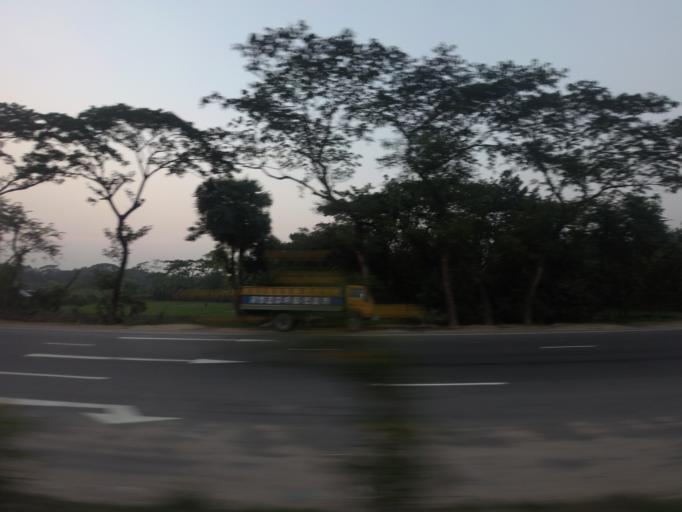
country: BD
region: Chittagong
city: Comilla
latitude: 23.4813
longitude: 91.0419
